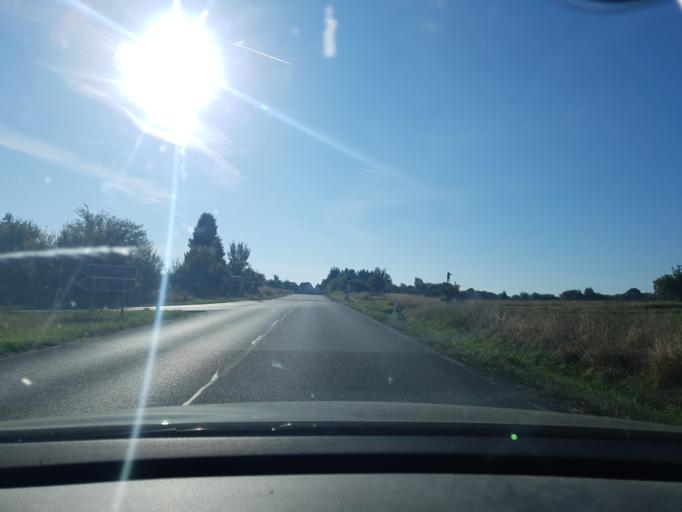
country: DE
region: Hesse
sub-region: Regierungsbezirk Darmstadt
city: Butzbach
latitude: 50.4641
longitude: 8.6425
